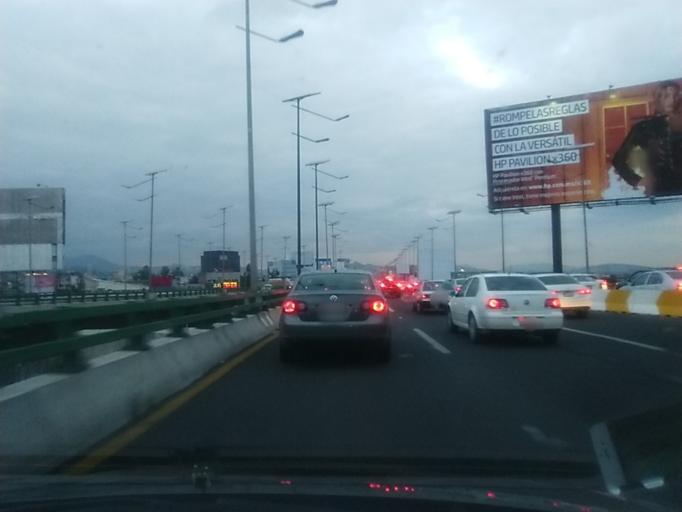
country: MX
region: Mexico
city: Naucalpan de Juarez
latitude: 19.4587
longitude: -99.2209
